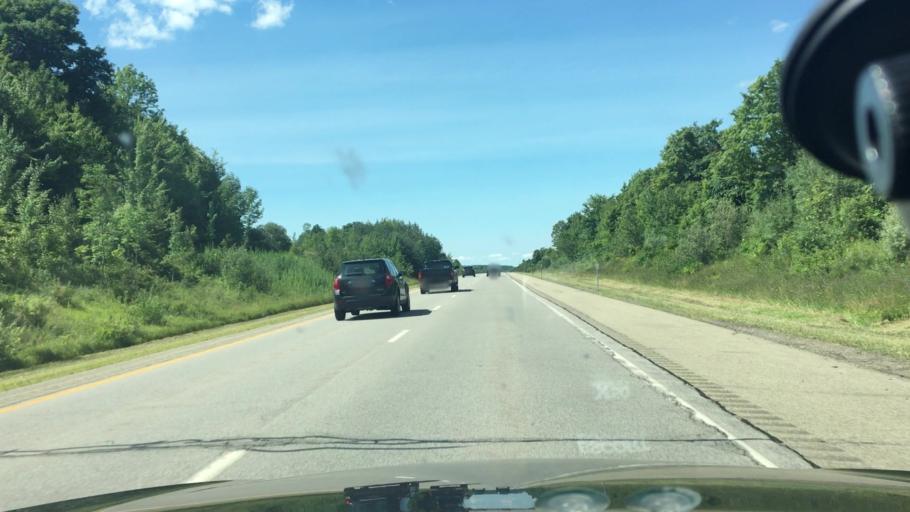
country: US
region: New York
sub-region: Erie County
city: Springville
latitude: 42.5826
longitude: -78.7269
